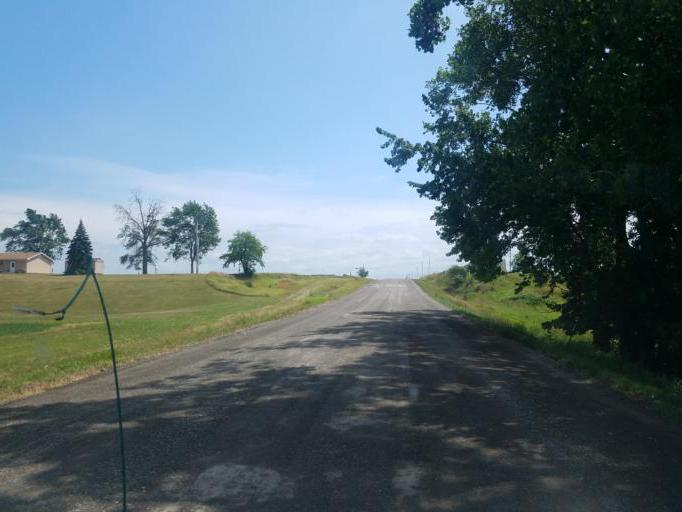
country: US
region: Indiana
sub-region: Allen County
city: Woodburn
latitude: 41.1654
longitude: -84.8490
